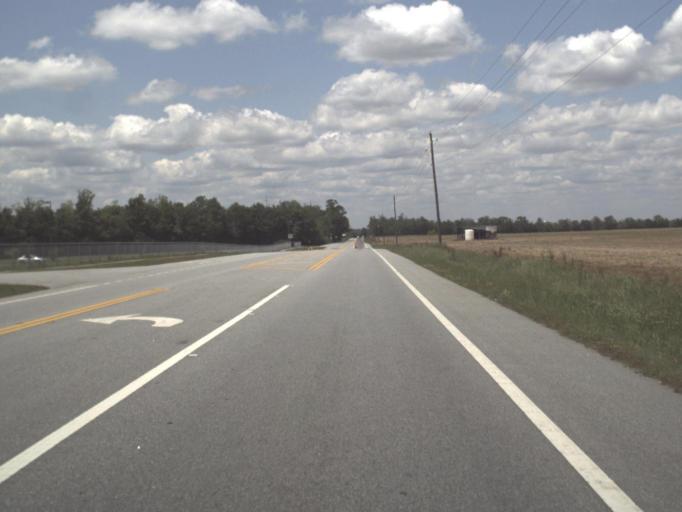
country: US
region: Florida
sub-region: Escambia County
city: Molino
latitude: 30.7413
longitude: -87.3614
